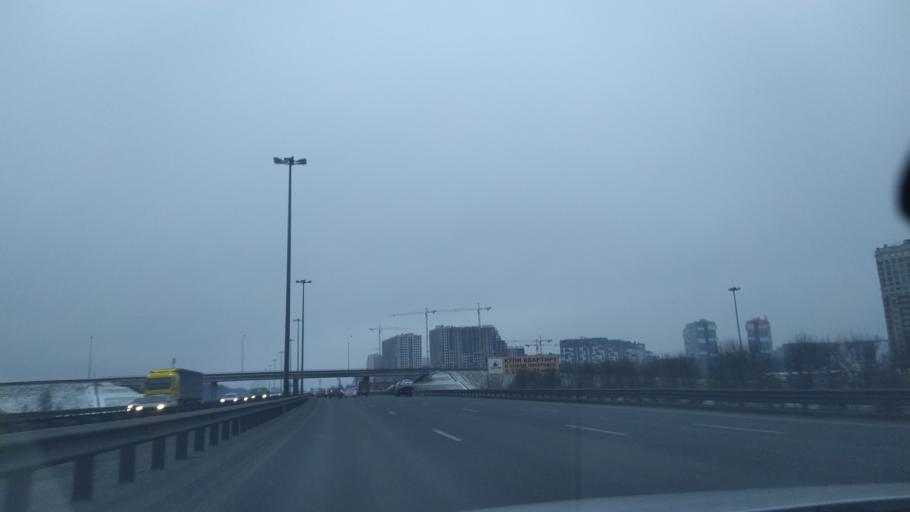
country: RU
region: St.-Petersburg
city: Krasnogvargeisky
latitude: 59.9176
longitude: 30.5256
